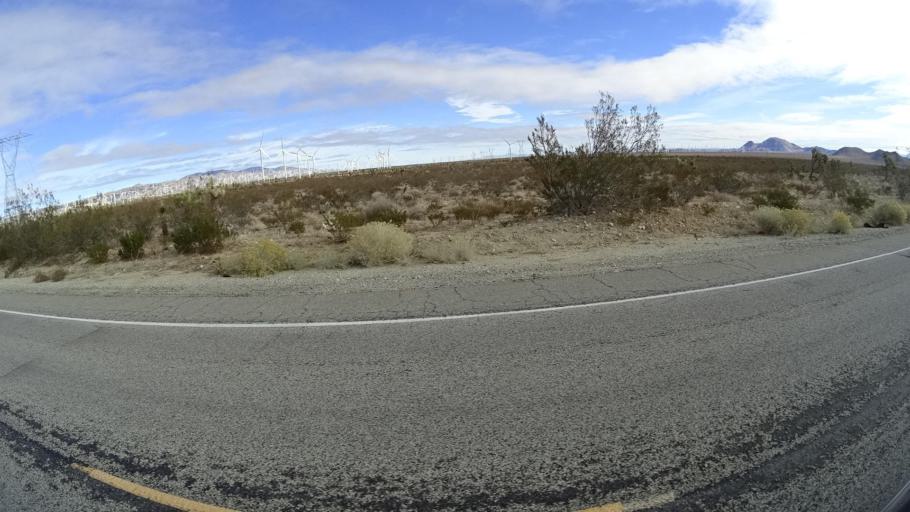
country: US
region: California
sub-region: Kern County
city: Mojave
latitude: 34.9885
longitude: -118.3219
